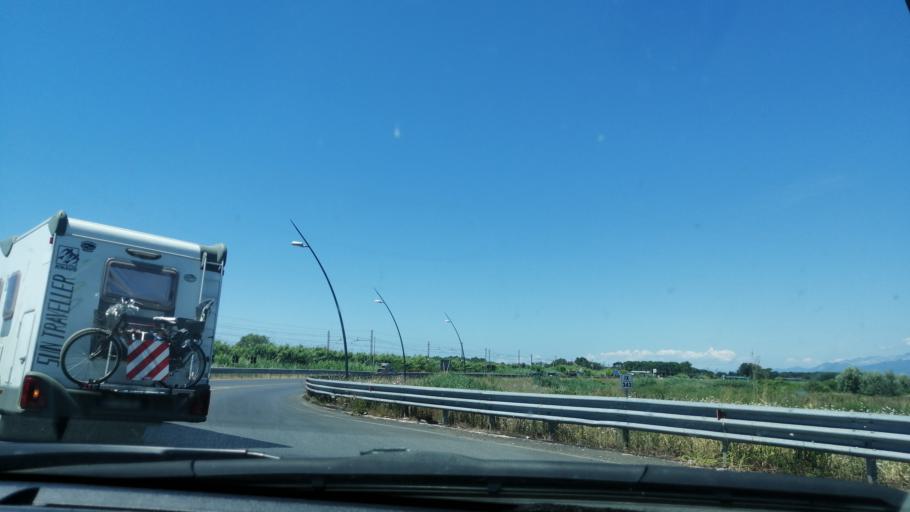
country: IT
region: Tuscany
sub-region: Province of Pisa
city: Migliarino
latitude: 43.7780
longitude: 10.3312
